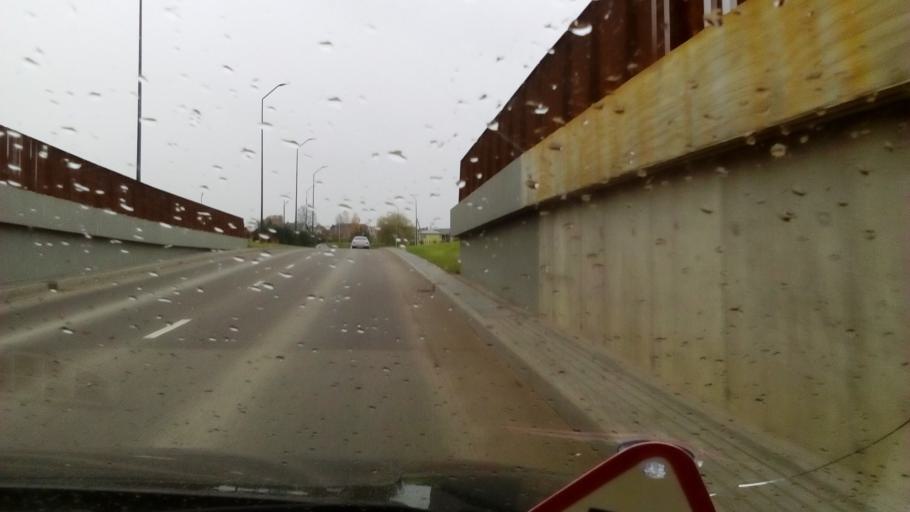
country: LT
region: Marijampoles apskritis
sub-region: Marijampole Municipality
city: Marijampole
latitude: 54.5443
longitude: 23.3558
